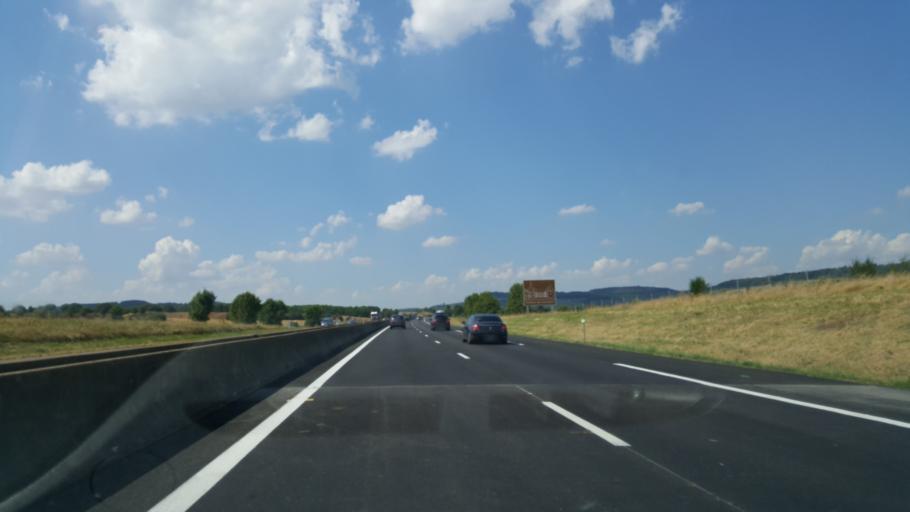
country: FR
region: Bourgogne
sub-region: Departement de la Cote-d'Or
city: Pouilly-en-Auxois
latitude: 47.2271
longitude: 4.5884
